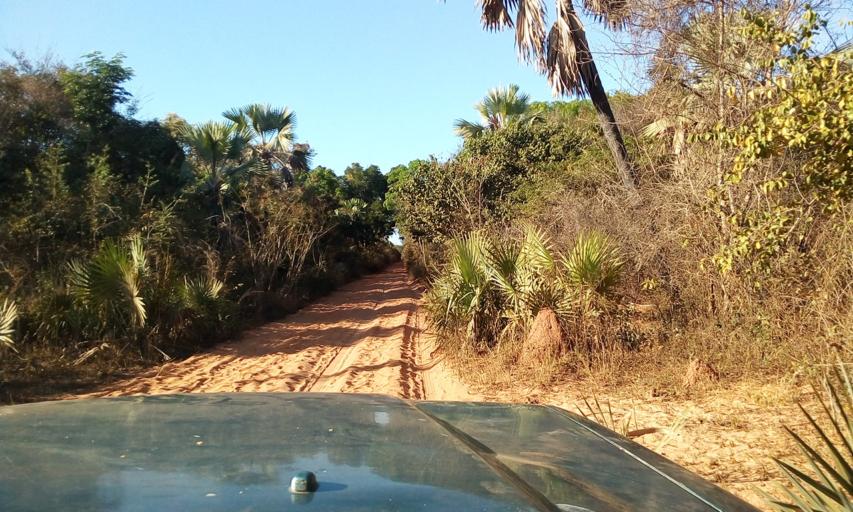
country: MG
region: Boeny
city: Sitampiky
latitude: -16.1653
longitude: 45.3557
